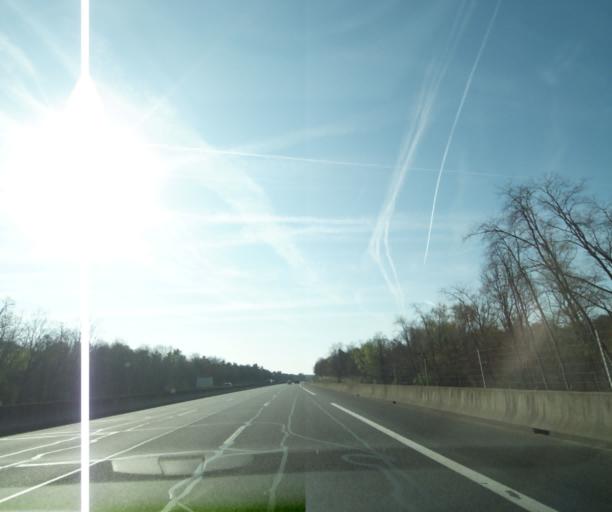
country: FR
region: Ile-de-France
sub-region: Departement de Seine-et-Marne
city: Bagneaux-sur-Loing
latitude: 48.2424
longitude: 2.7472
